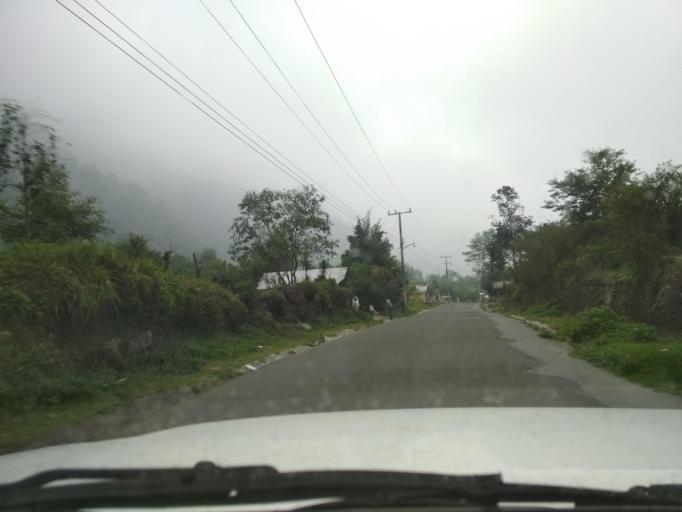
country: MX
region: Veracruz
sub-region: Mariano Escobedo
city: San Isidro el Berro
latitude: 18.9552
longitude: -97.1774
